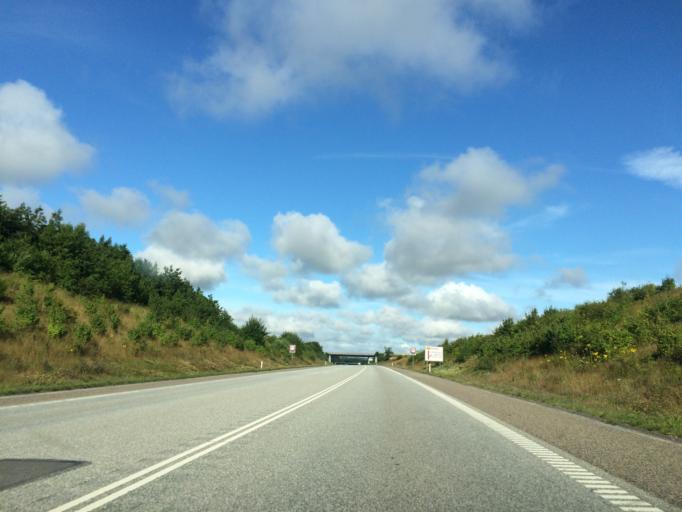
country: DK
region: Central Jutland
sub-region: Silkeborg Kommune
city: Kjellerup
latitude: 56.3598
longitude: 9.5124
